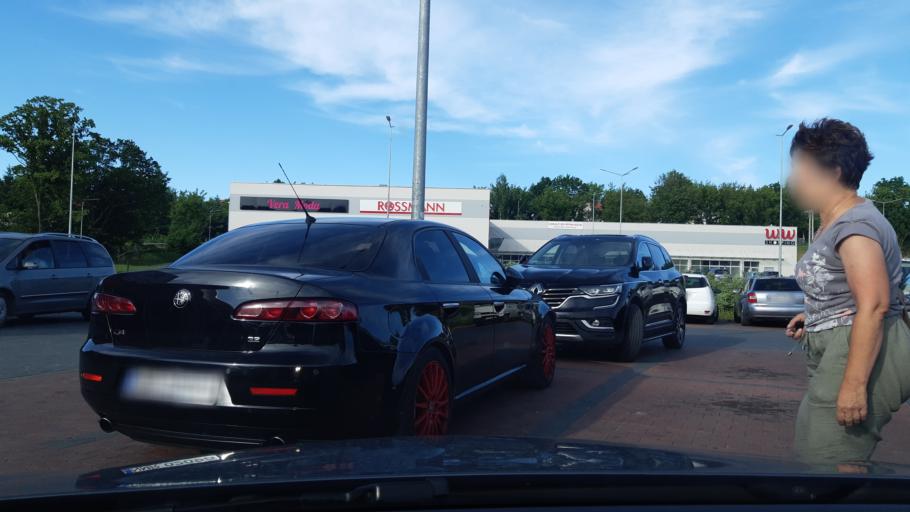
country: PL
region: Warmian-Masurian Voivodeship
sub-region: Powiat mragowski
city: Mragowo
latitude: 53.8786
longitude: 21.3067
